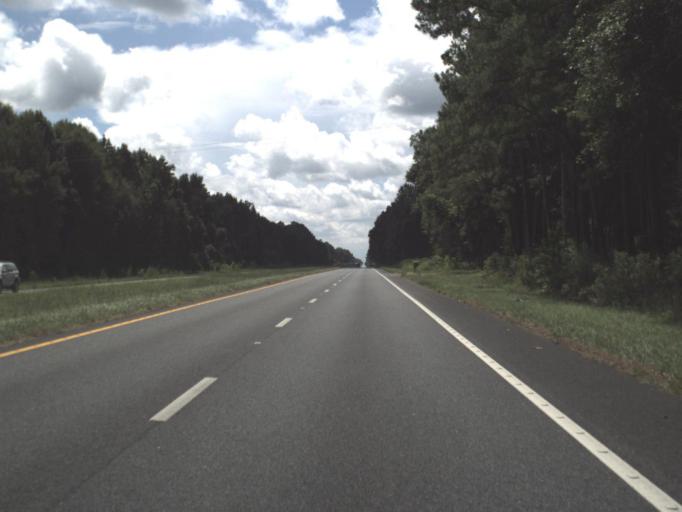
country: US
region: Florida
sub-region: Taylor County
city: Perry
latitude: 30.2979
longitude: -83.7434
